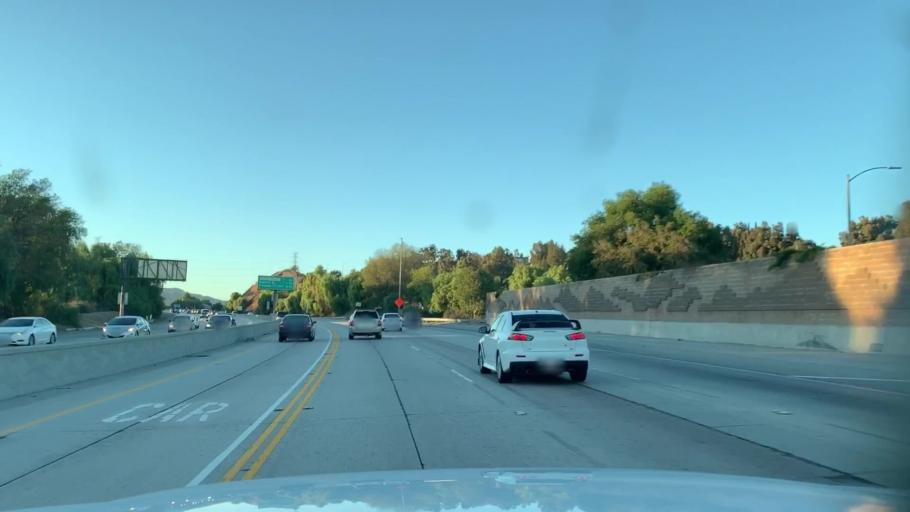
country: US
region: California
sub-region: Los Angeles County
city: San Fernando
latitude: 34.2839
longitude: -118.4583
